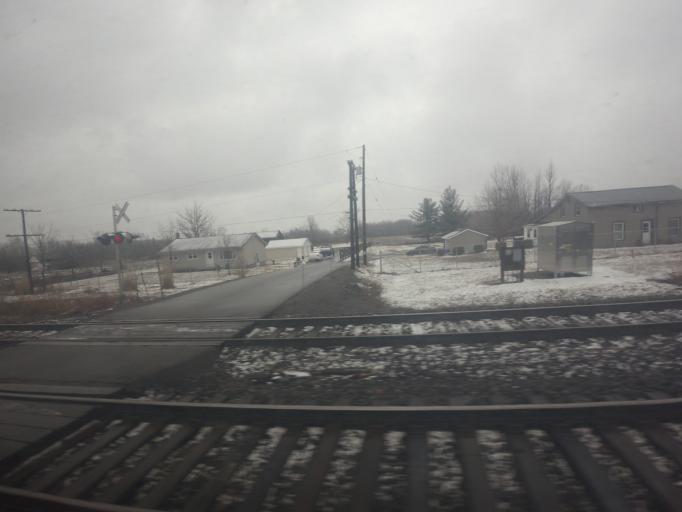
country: CA
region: Ontario
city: Belleville
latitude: 44.1927
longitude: -77.3223
